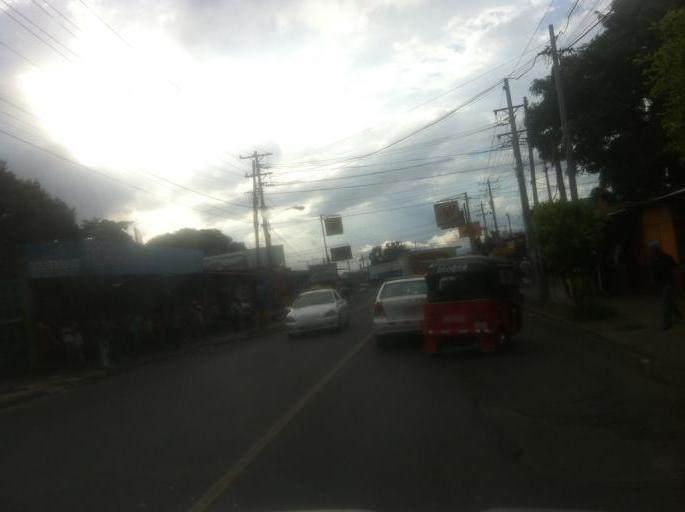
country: NI
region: Managua
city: Managua
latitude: 12.1215
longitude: -86.2433
